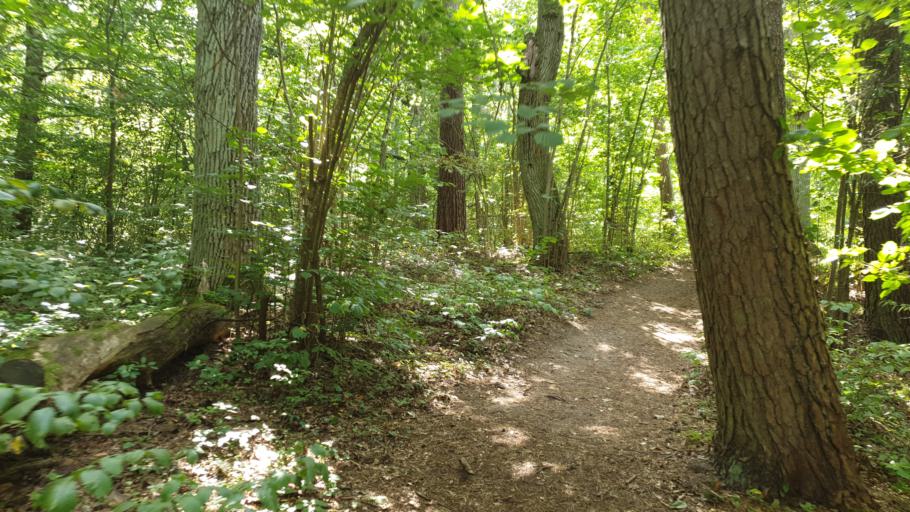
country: LT
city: Grigiskes
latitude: 54.7999
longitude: 24.9815
